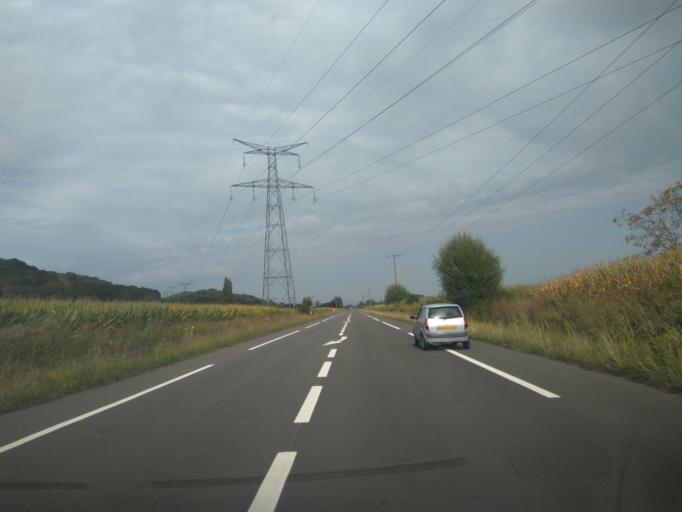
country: FR
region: Aquitaine
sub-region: Departement des Pyrenees-Atlantiques
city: Arbus
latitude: 43.3408
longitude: -0.5114
